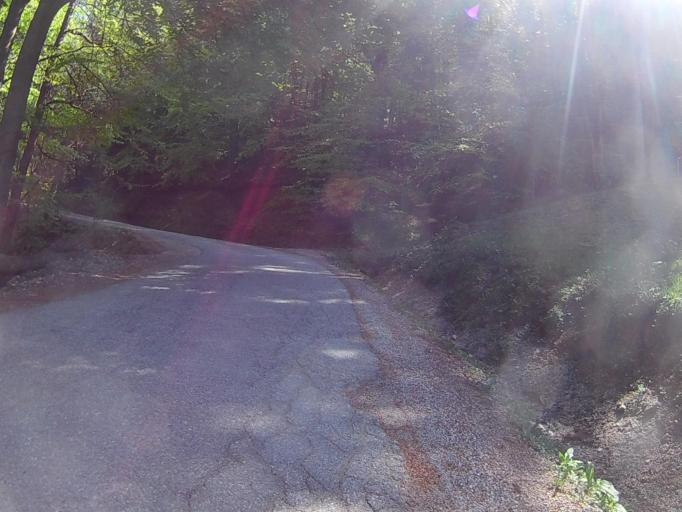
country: SI
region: Ruse
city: Ruse
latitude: 46.5259
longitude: 15.5135
